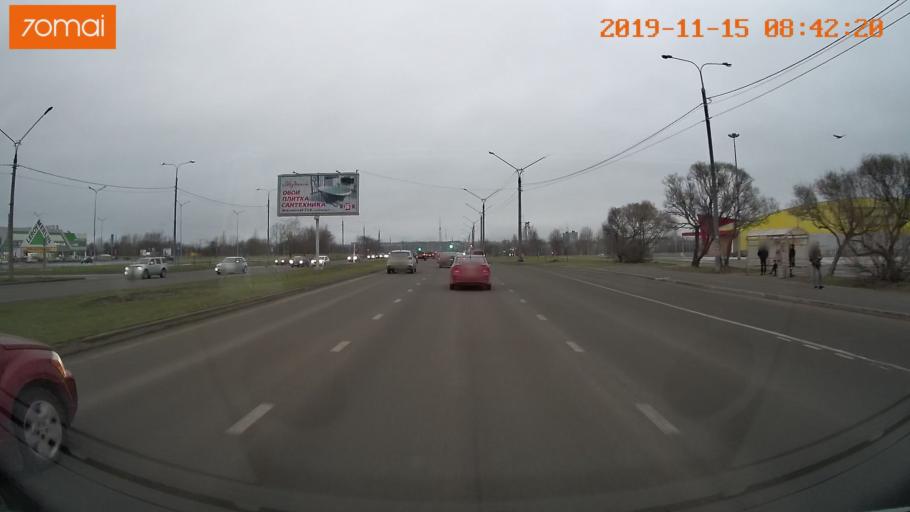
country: RU
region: Vologda
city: Cherepovets
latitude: 59.1022
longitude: 37.9085
